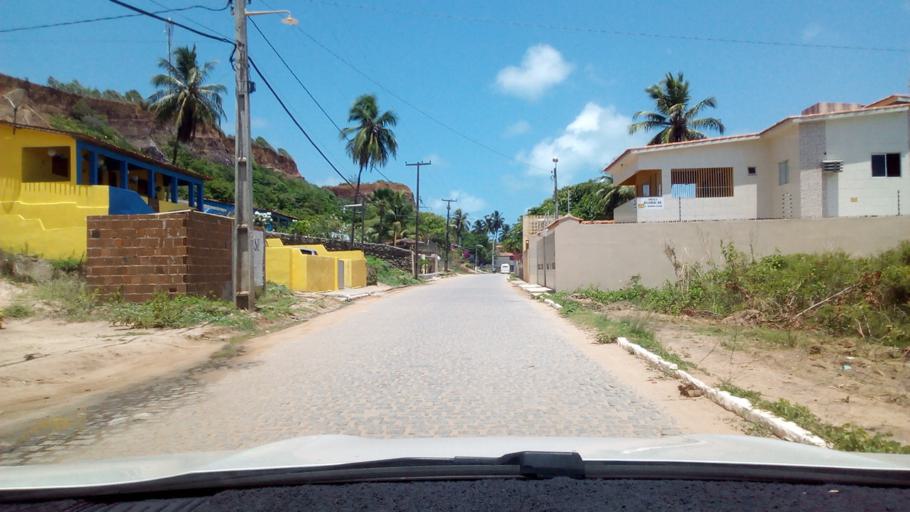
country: BR
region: Paraiba
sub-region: Pitimbu
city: Pitimbu
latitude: -7.4830
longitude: -34.8144
